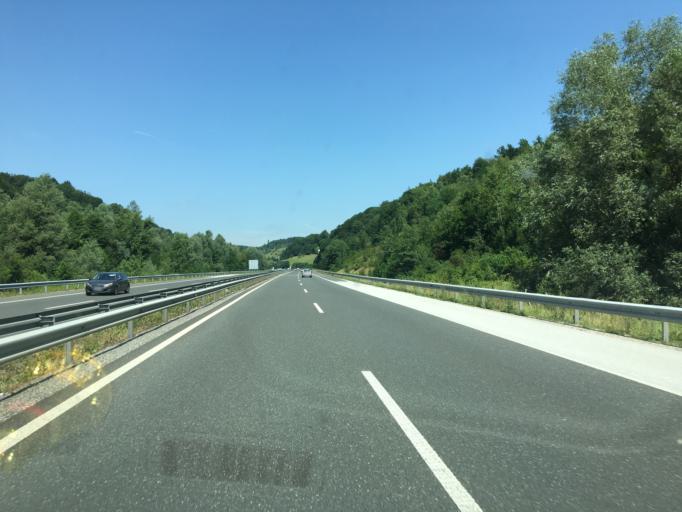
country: SI
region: Pesnica
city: Pesnica pri Mariboru
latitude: 46.6255
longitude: 15.6577
